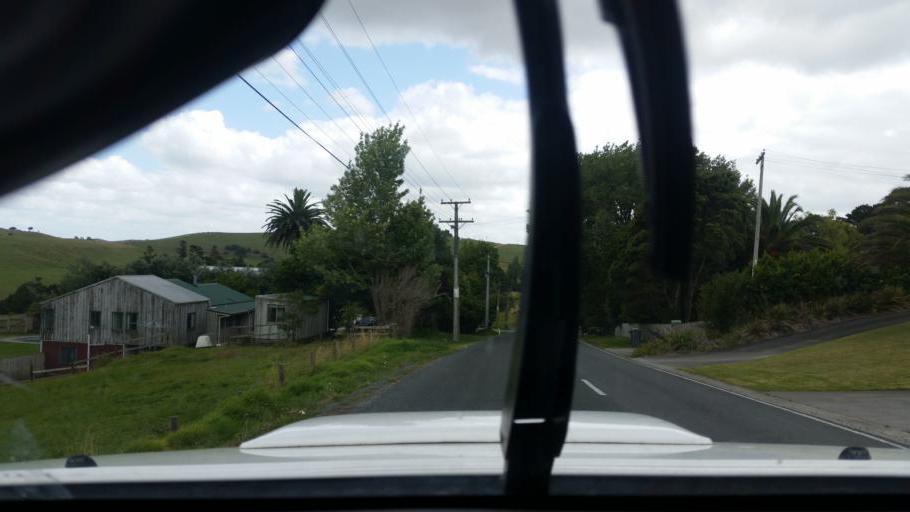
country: NZ
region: Northland
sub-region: Whangarei
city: Ruakaka
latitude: -36.0999
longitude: 174.3509
